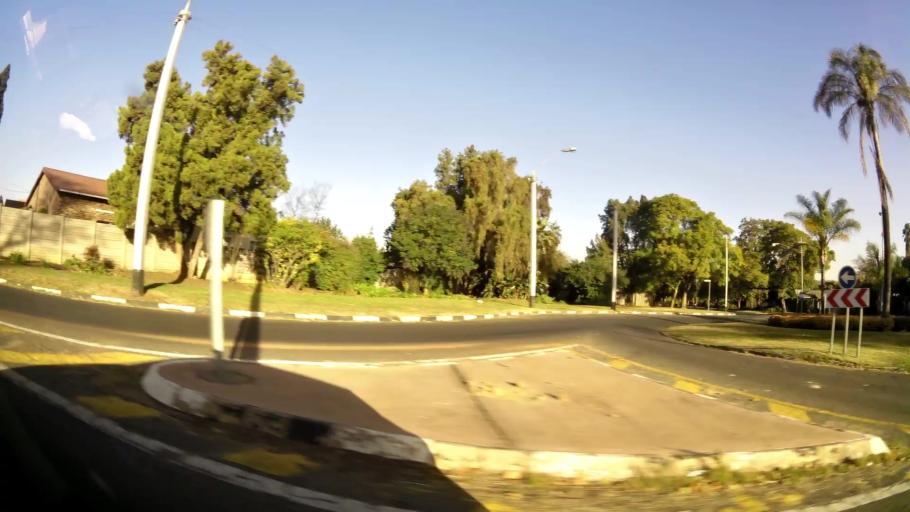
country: ZA
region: Gauteng
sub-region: City of Tshwane Metropolitan Municipality
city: Pretoria
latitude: -25.7006
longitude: 28.2173
